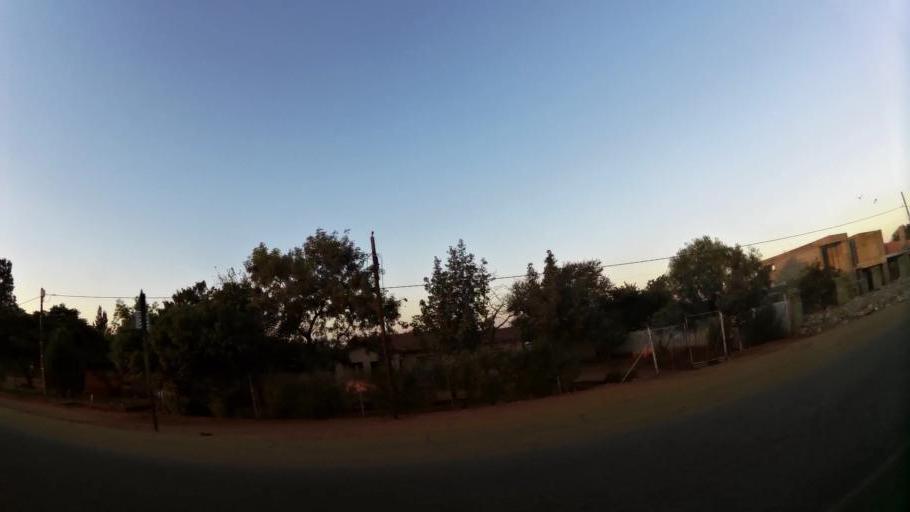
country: ZA
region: North-West
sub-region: Bojanala Platinum District Municipality
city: Rustenburg
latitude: -25.6096
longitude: 27.1886
